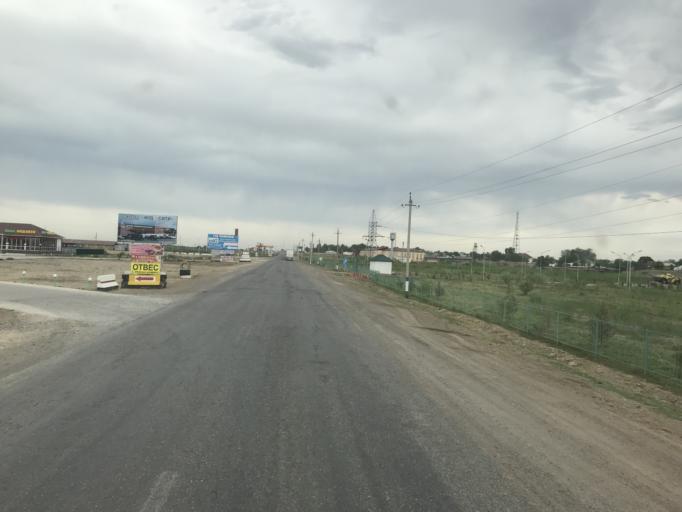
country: KZ
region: Ongtustik Qazaqstan
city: Asykata
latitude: 40.9628
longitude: 68.4598
